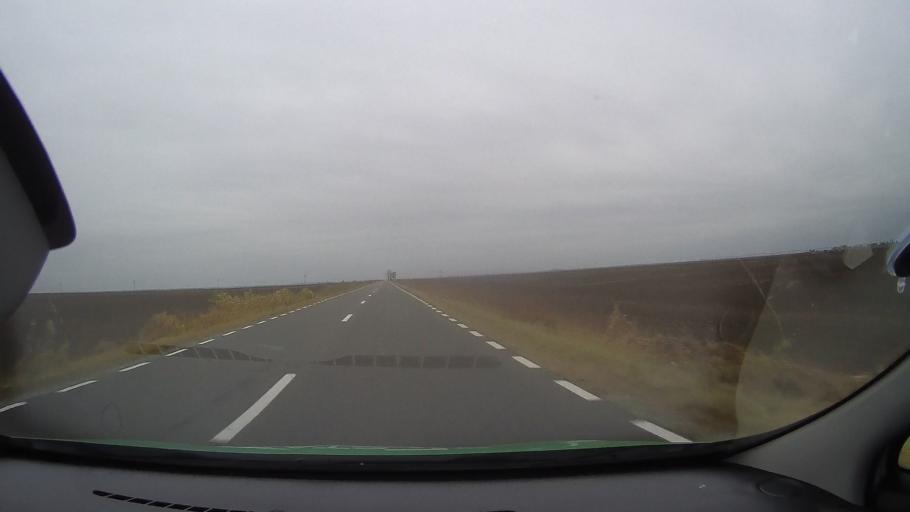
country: RO
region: Ialomita
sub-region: Comuna Gheorghe Lazar
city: Gheorghe Lazar
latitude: 44.6643
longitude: 27.4148
